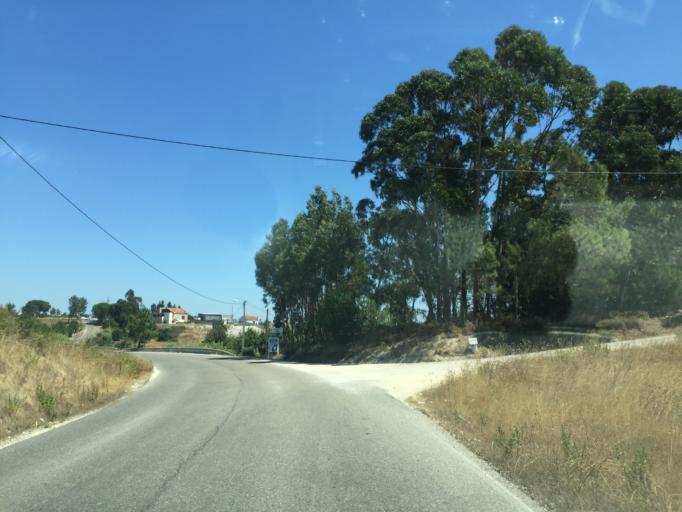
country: PT
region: Lisbon
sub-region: Azambuja
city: Aveiras de Cima
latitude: 39.1519
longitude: -8.8859
